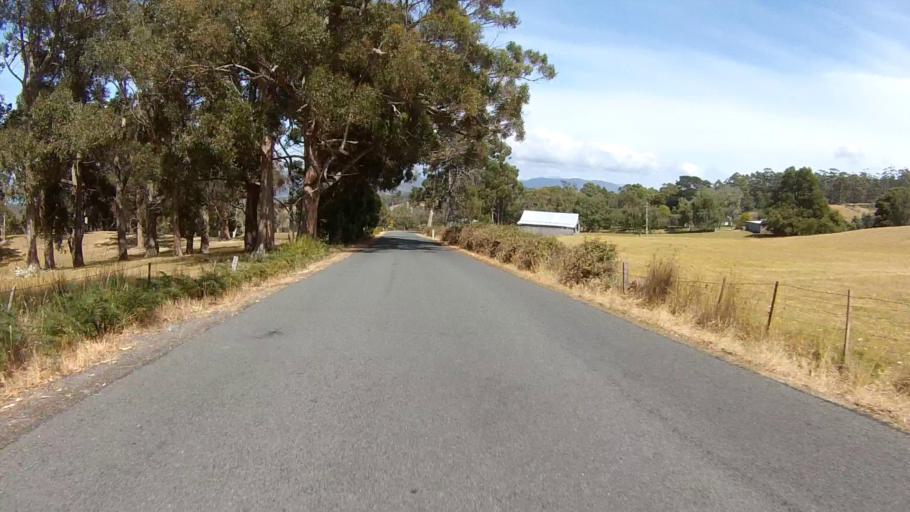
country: AU
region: Tasmania
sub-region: Huon Valley
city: Cygnet
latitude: -43.2324
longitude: 147.1289
